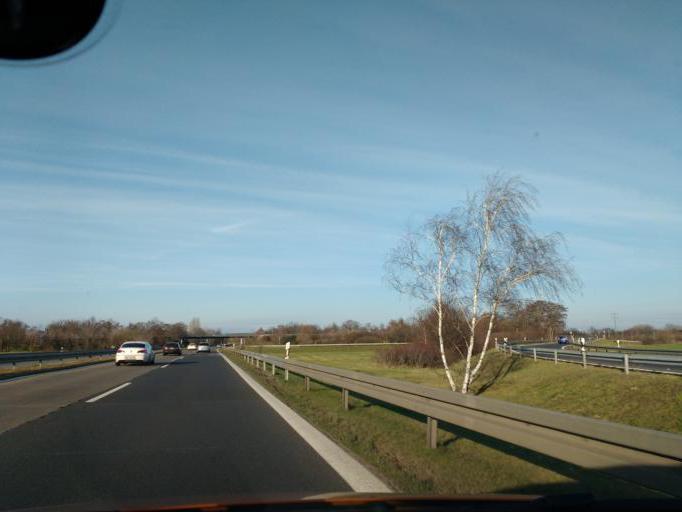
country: DE
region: Berlin
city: Buchholz
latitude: 52.6212
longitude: 13.4344
